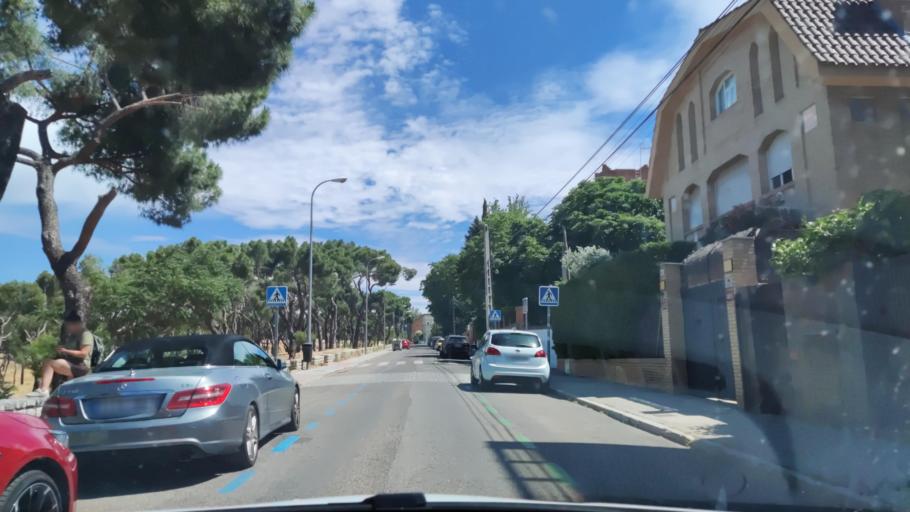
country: ES
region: Madrid
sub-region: Provincia de Madrid
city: Tetuan de las Victorias
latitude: 40.4543
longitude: -3.7181
